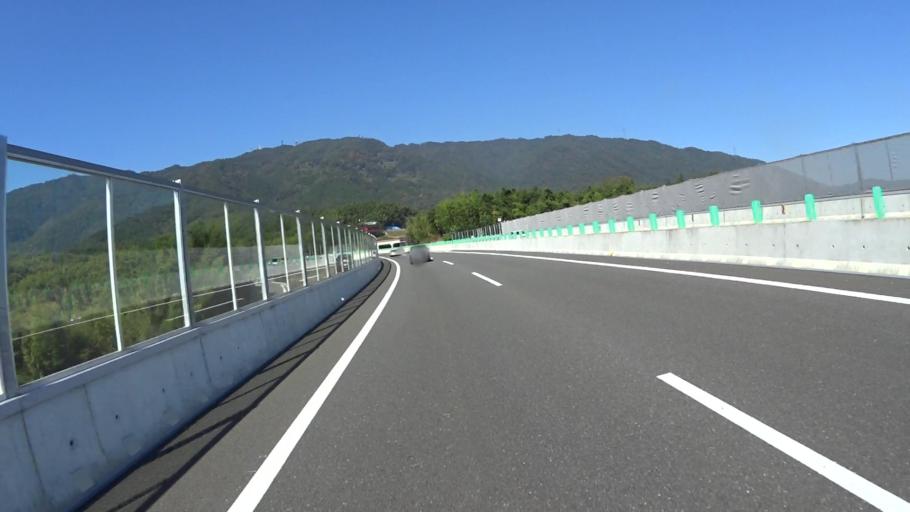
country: JP
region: Kyoto
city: Muko
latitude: 34.9533
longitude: 135.6596
